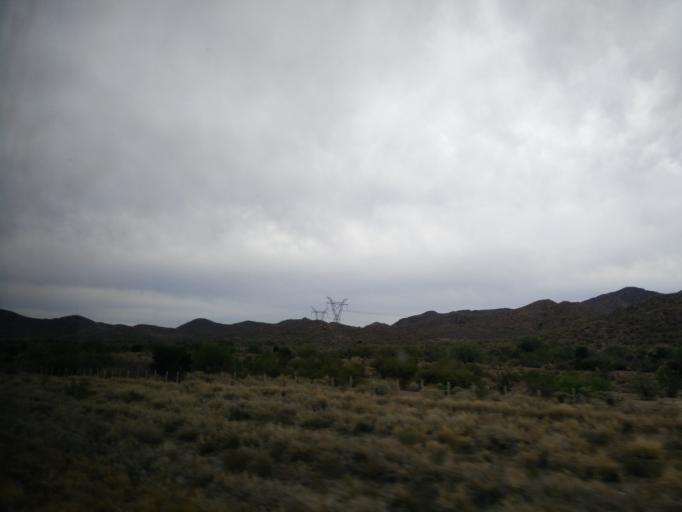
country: MX
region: Sonora
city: Hermosillo
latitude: 28.6125
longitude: -111.0167
